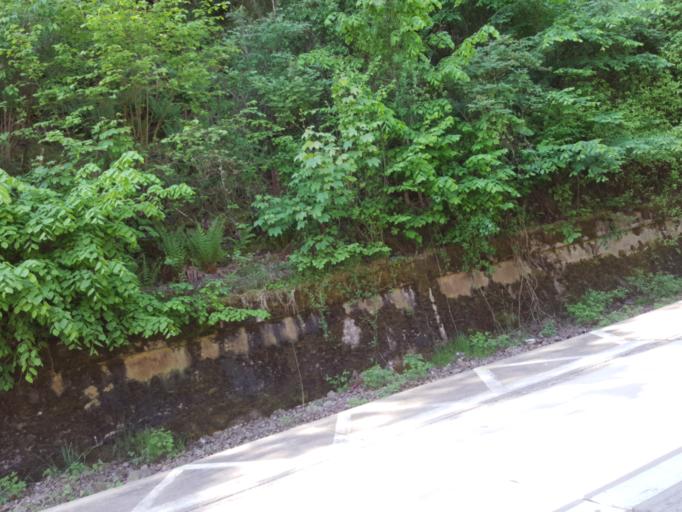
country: SE
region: Skane
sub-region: Bastads Kommun
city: Bastad
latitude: 56.4251
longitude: 12.8693
